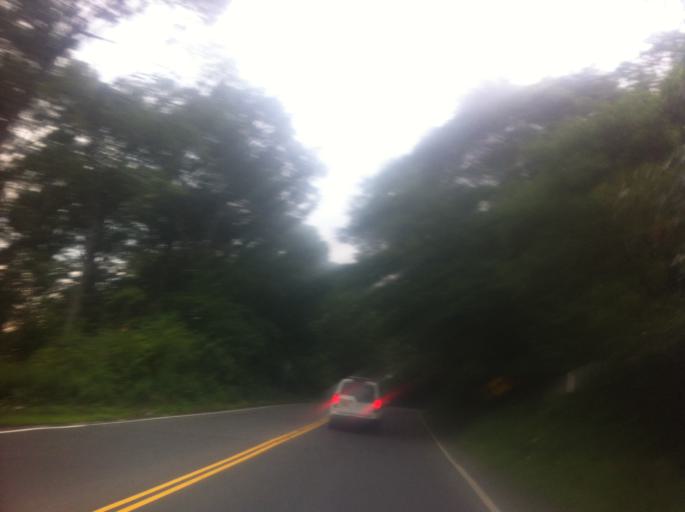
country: US
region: New York
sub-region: Nassau County
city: Bethpage
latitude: 40.7338
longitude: -73.4701
